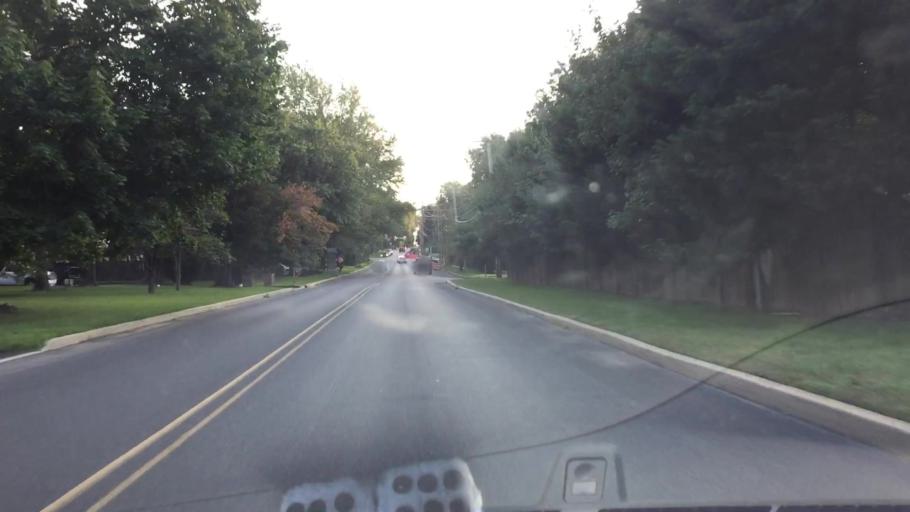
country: US
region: Pennsylvania
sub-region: Montgomery County
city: Blue Bell
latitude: 40.1449
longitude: -75.2965
